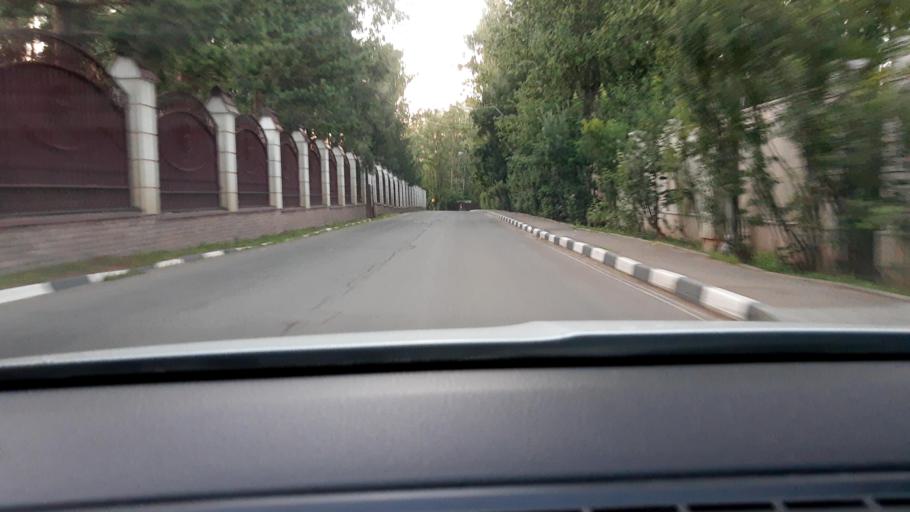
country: RU
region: Moskovskaya
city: Zarech'ye
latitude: 55.6849
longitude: 37.3843
